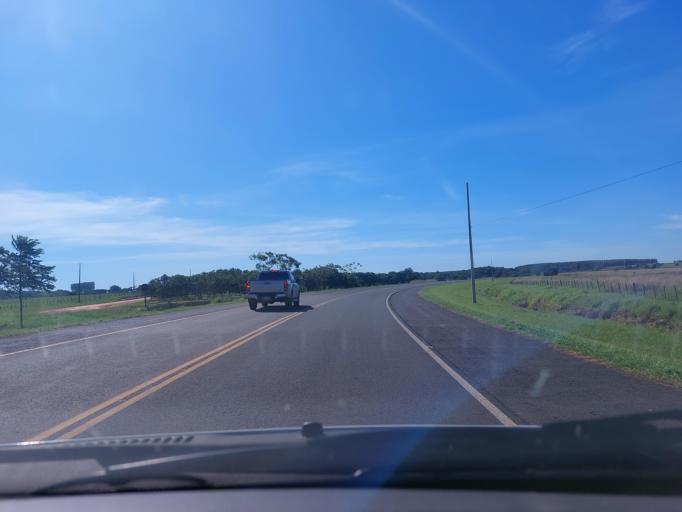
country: PY
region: San Pedro
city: Itacurubi del Rosario
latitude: -24.6028
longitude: -56.7834
